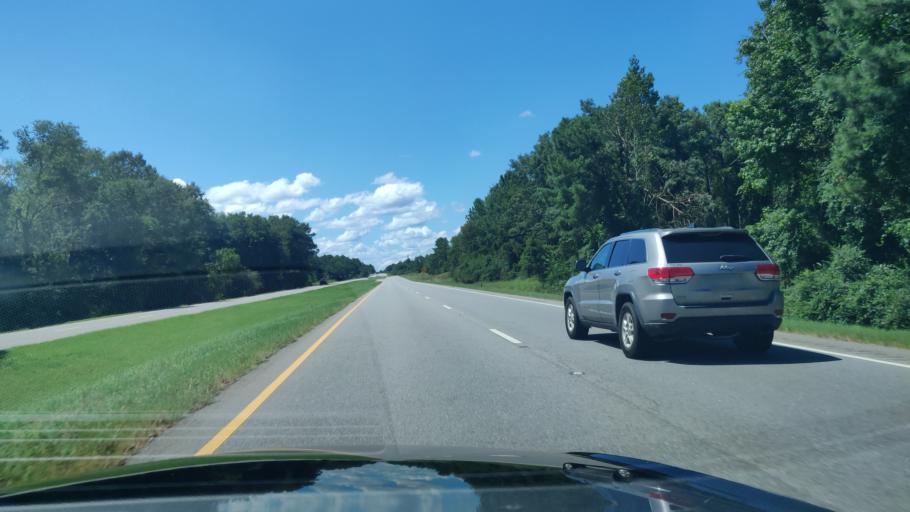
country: US
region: Georgia
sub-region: Terrell County
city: Dawson
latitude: 31.8819
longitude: -84.5023
